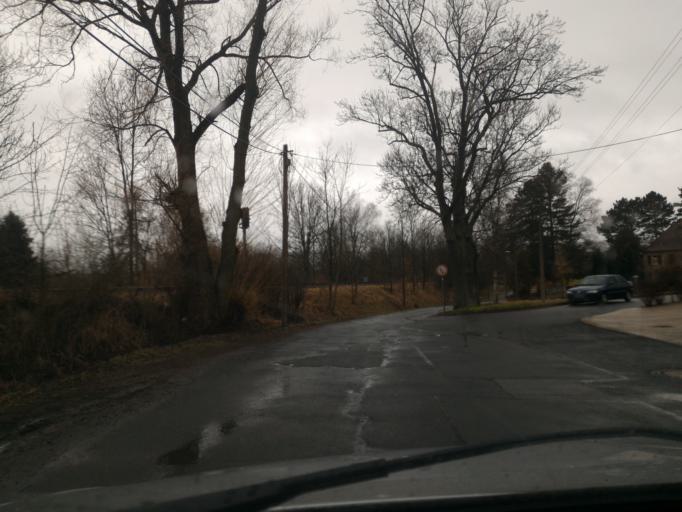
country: DE
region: Saxony
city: Seifhennersdorf
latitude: 50.9309
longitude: 14.6092
